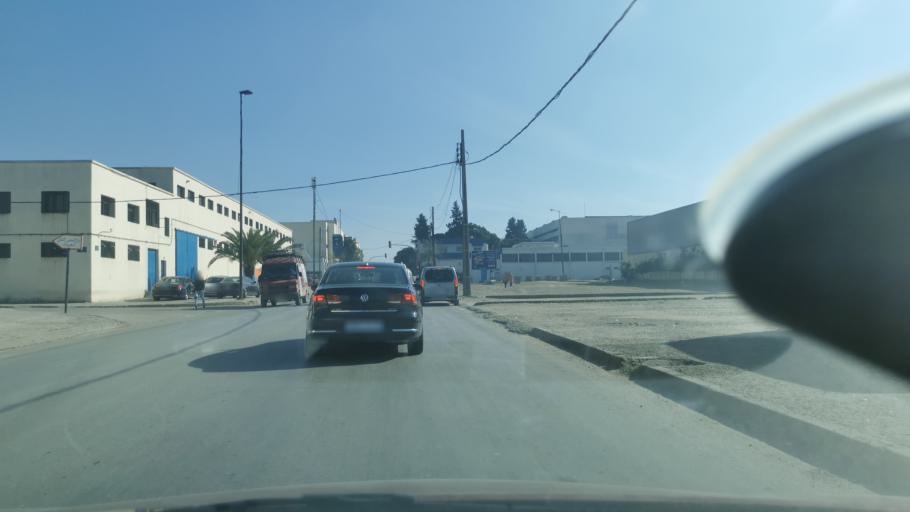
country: MA
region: Fes-Boulemane
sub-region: Fes
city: Fes
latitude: 34.0264
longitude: -4.9775
